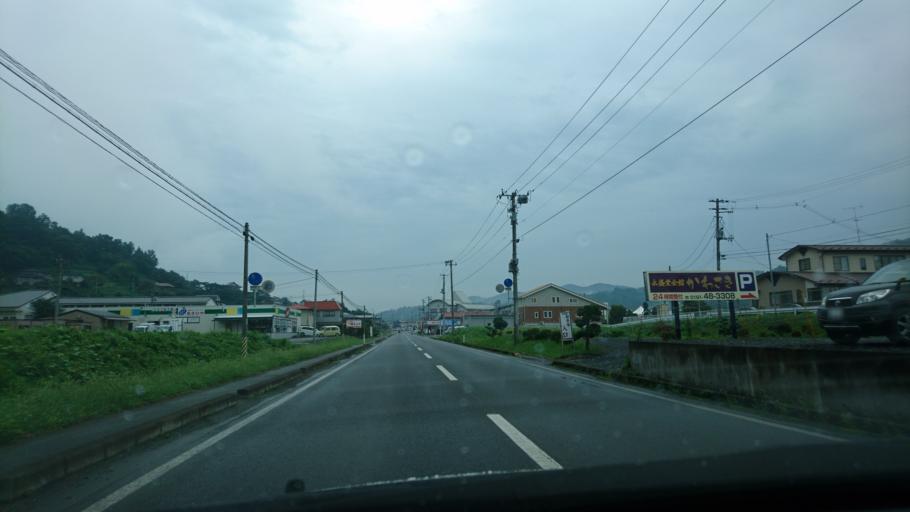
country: JP
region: Iwate
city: Ichinoseki
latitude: 38.9002
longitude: 141.2721
